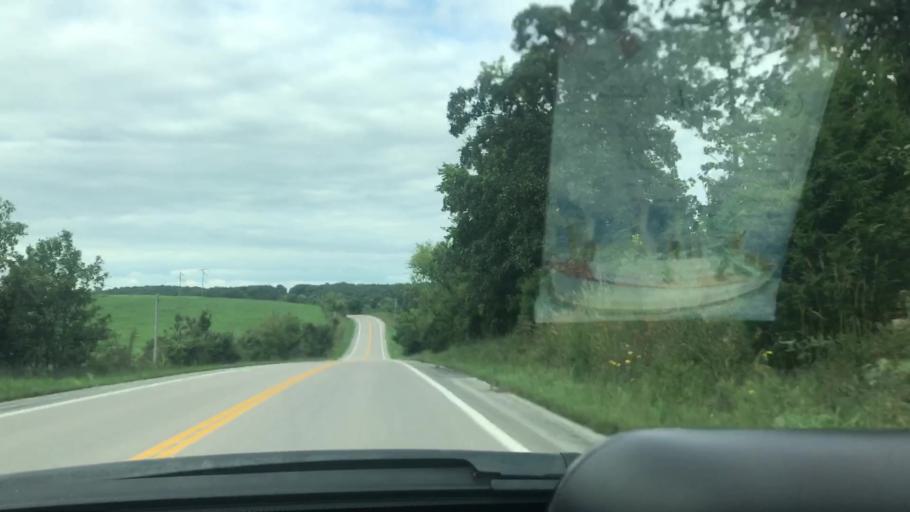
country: US
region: Missouri
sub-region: Benton County
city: Warsaw
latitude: 38.1277
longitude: -93.2805
